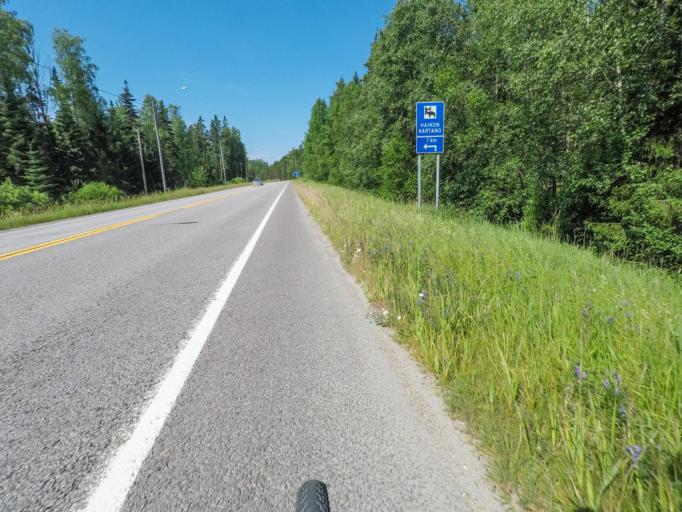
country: FI
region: Uusimaa
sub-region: Porvoo
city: Porvoo
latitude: 60.3714
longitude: 25.5748
